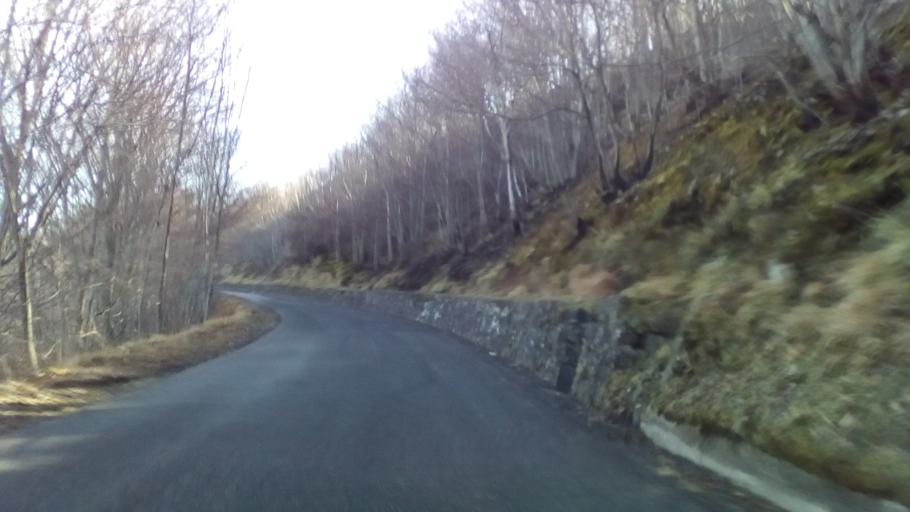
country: IT
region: Tuscany
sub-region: Provincia di Lucca
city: Castiglione di Garfagnana
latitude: 44.1652
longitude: 10.4468
